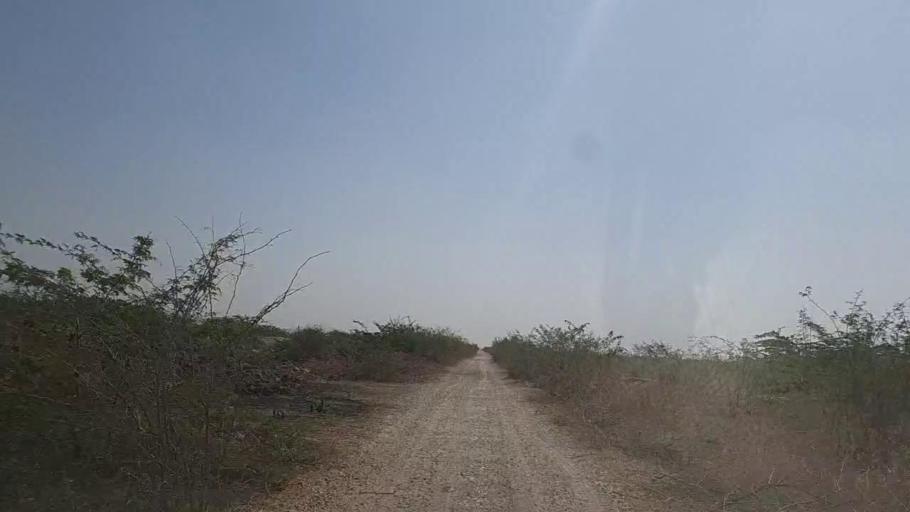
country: PK
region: Sindh
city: Naukot
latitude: 24.6403
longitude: 69.2741
